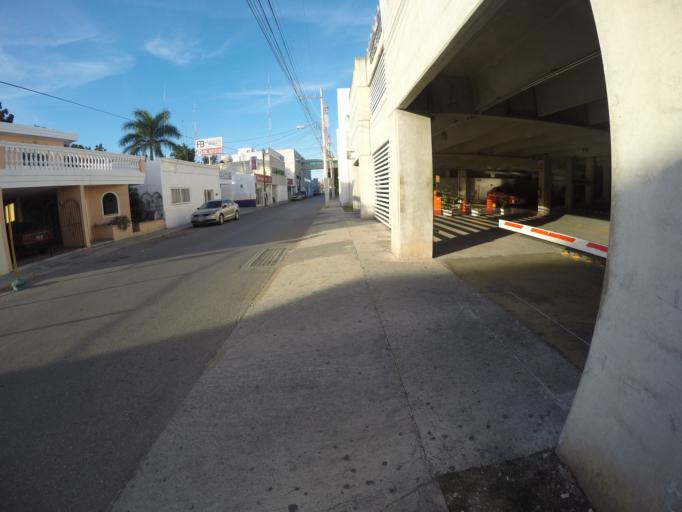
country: MX
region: Yucatan
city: Merida
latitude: 20.9833
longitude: -89.6160
